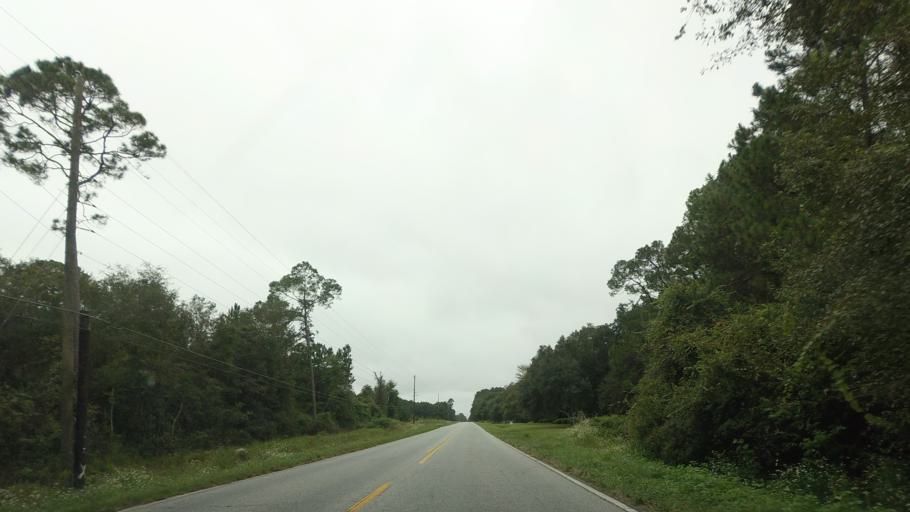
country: US
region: Georgia
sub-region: Lowndes County
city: Valdosta
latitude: 30.8135
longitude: -83.2416
